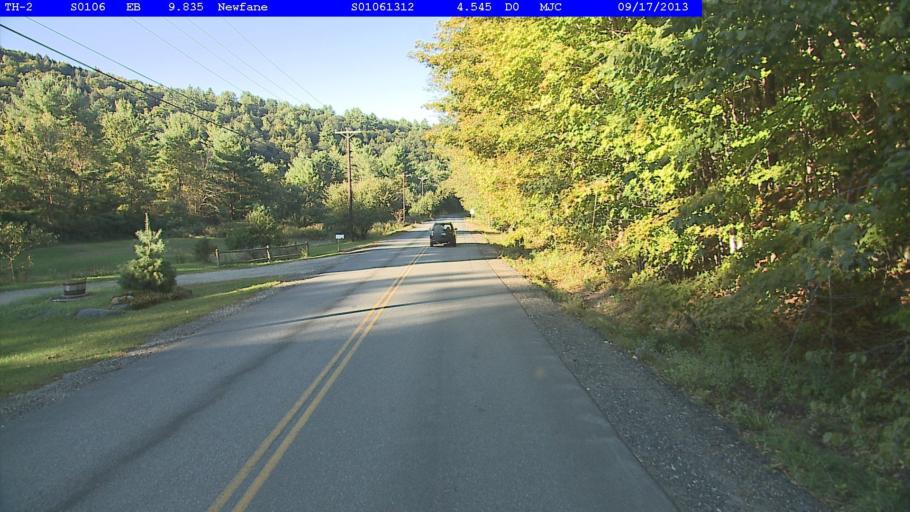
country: US
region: Vermont
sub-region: Windham County
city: Newfane
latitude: 42.9397
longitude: -72.6912
